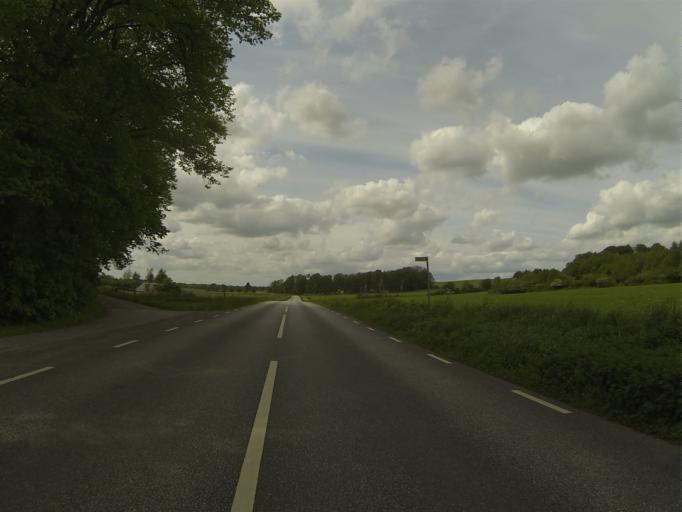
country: SE
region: Skane
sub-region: Sjobo Kommun
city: Sjoebo
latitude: 55.6740
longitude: 13.6608
